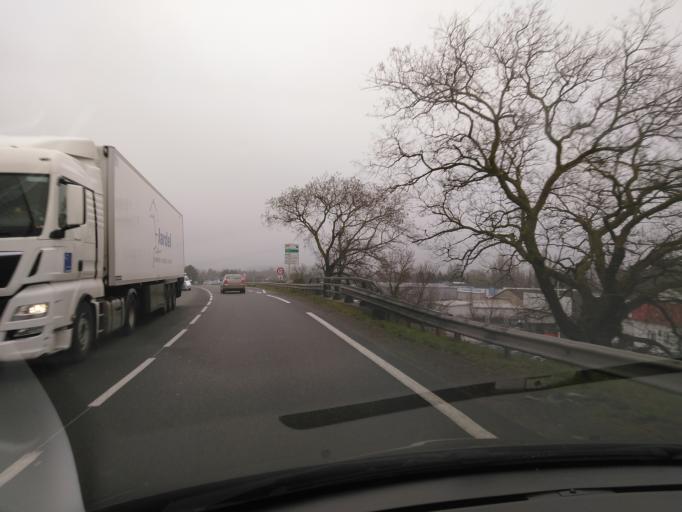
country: FR
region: Languedoc-Roussillon
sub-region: Departement de l'Aude
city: Carcassonne
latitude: 43.2143
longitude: 2.3223
